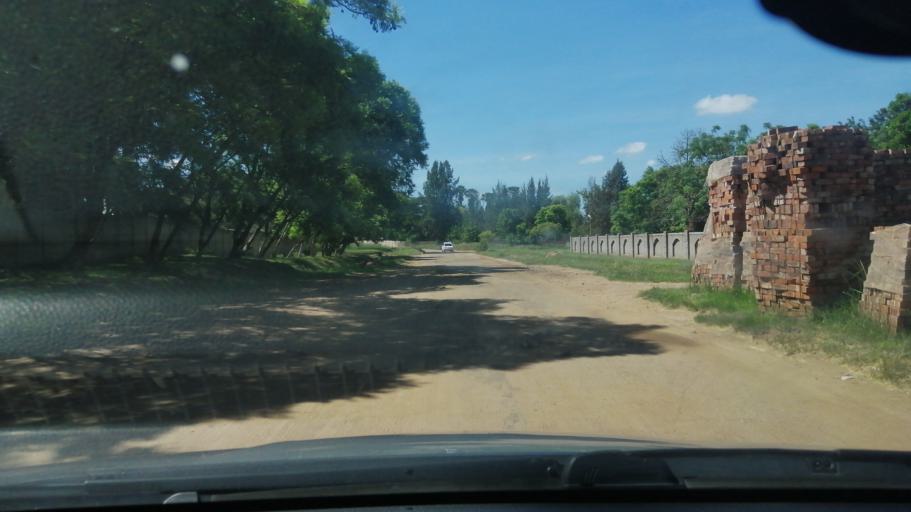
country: ZW
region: Harare
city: Harare
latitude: -17.8160
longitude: 31.1288
